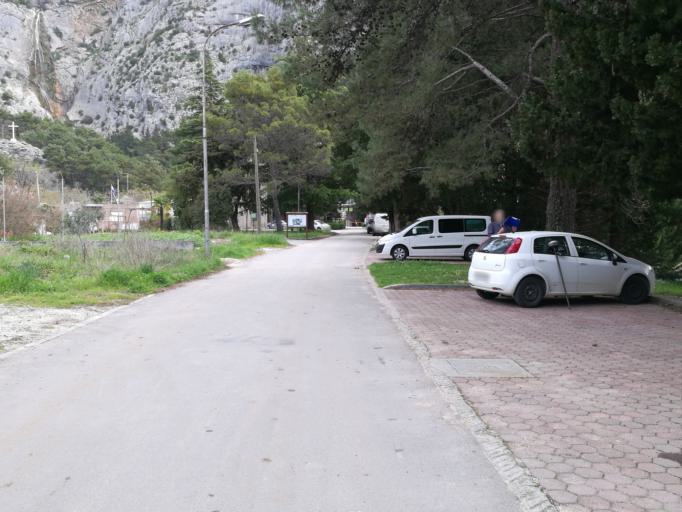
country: HR
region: Splitsko-Dalmatinska
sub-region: Grad Omis
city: Omis
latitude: 43.4563
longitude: 16.7003
